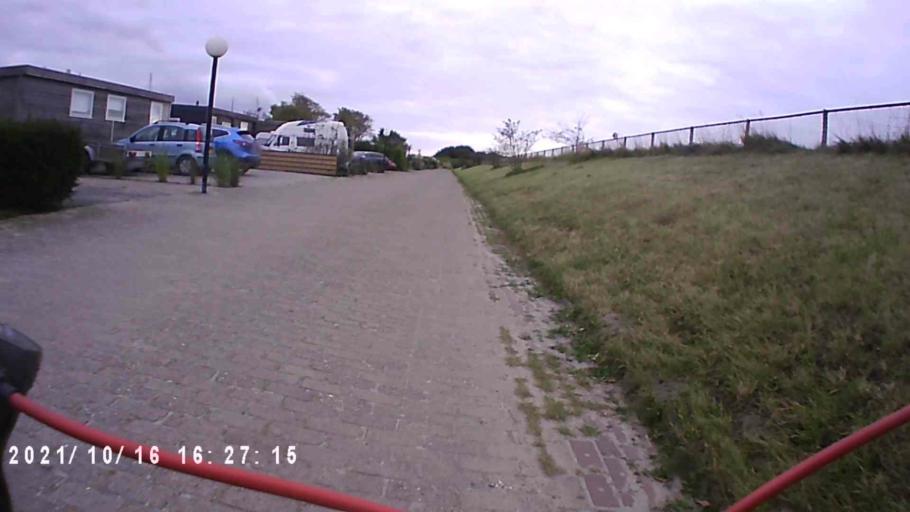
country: NL
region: Friesland
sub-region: Gemeente Dongeradeel
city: Anjum
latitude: 53.3844
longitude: 6.1567
